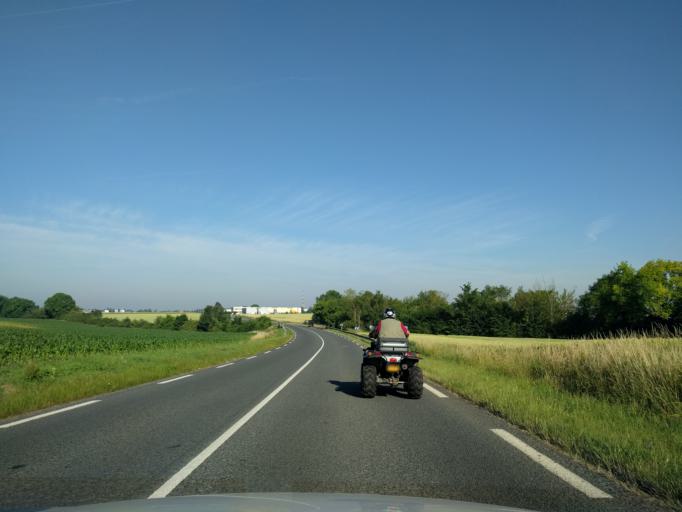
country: FR
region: Picardie
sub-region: Departement de la Somme
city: Montdidier
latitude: 49.6473
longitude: 2.6027
